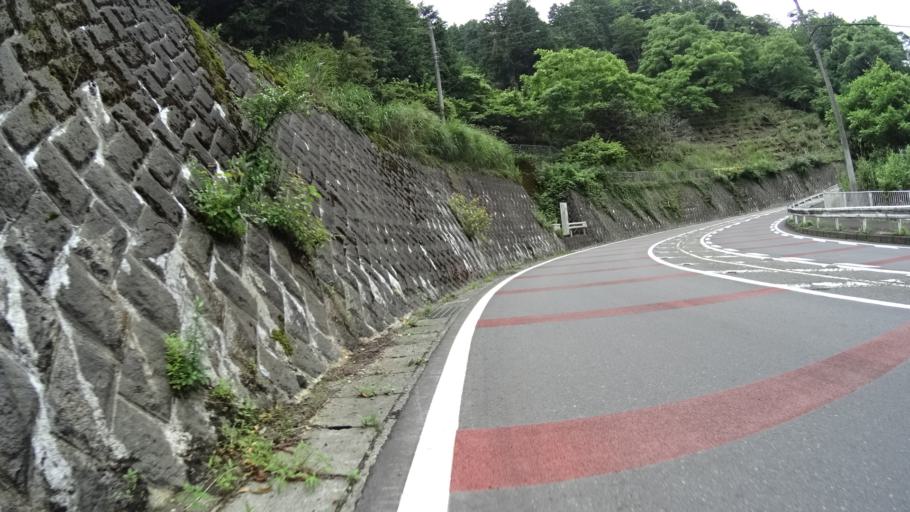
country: JP
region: Kanagawa
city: Atsugi
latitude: 35.5014
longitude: 139.2576
